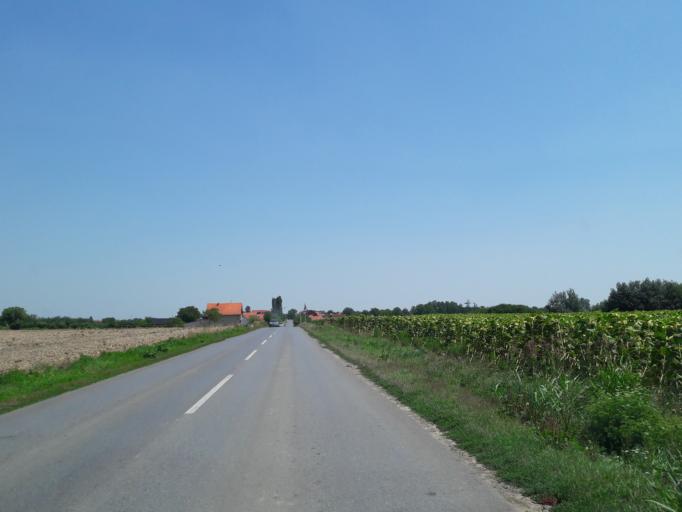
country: HR
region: Osjecko-Baranjska
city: Viskovci
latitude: 45.3448
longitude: 18.4400
